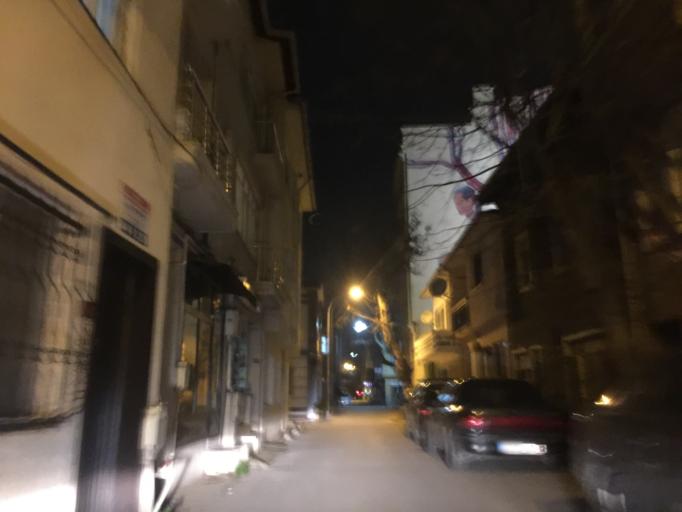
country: TR
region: Istanbul
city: Icmeler
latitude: 40.8160
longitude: 29.3050
